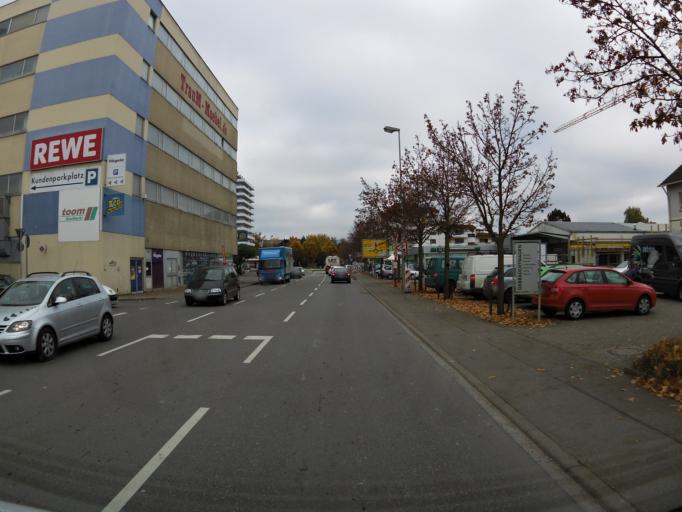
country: DE
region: Baden-Wuerttemberg
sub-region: Freiburg Region
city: Radolfzell am Bodensee
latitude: 47.7440
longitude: 8.9579
